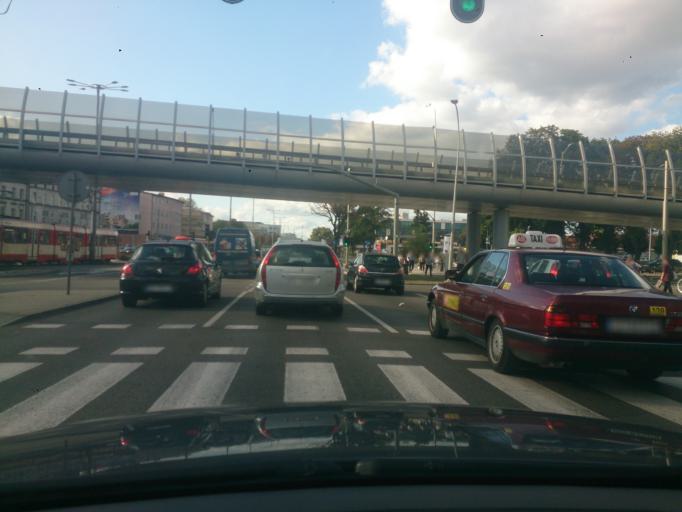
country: PL
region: Pomeranian Voivodeship
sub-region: Gdansk
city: Gdansk
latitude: 54.3825
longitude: 18.5988
